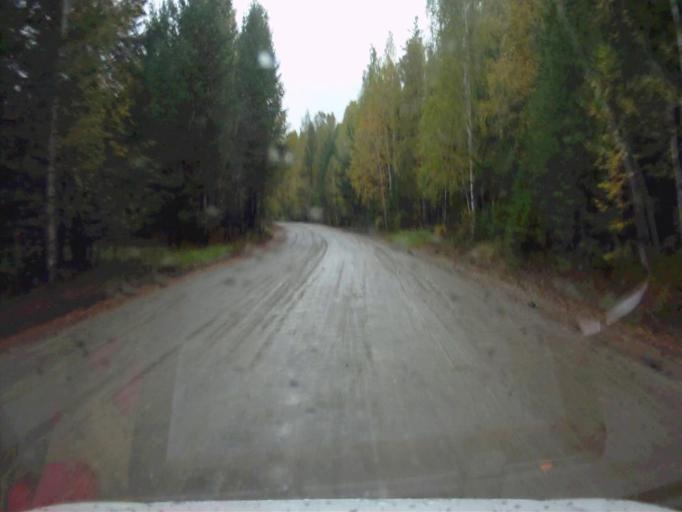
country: RU
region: Chelyabinsk
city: Kyshtym
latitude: 55.7482
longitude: 60.4893
